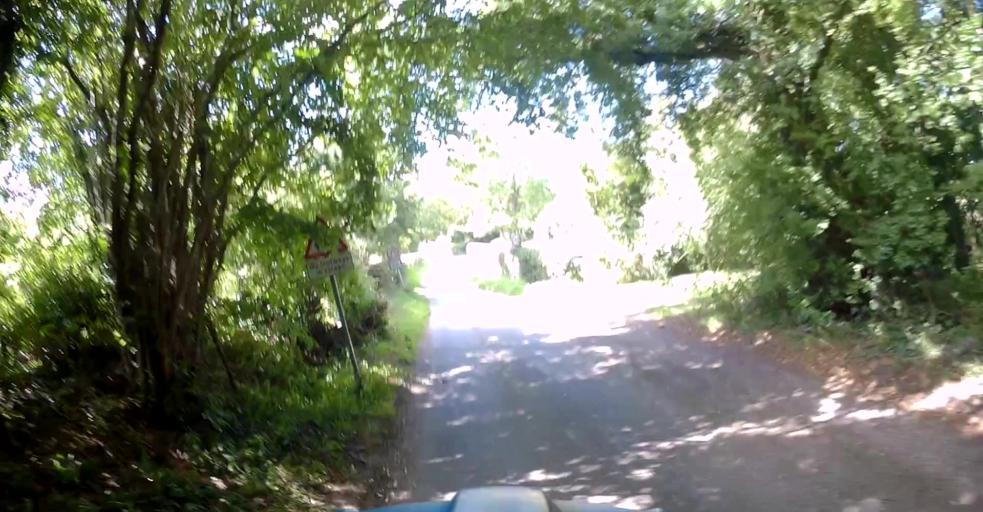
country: GB
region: England
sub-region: Hampshire
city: Four Marks
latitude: 51.1525
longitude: -1.0898
